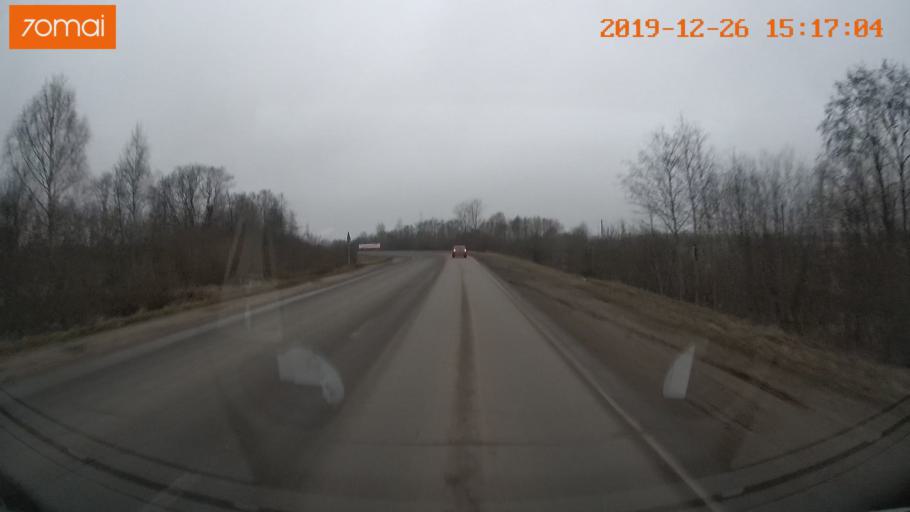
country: RU
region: Jaroslavl
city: Rybinsk
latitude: 58.0802
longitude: 38.8548
